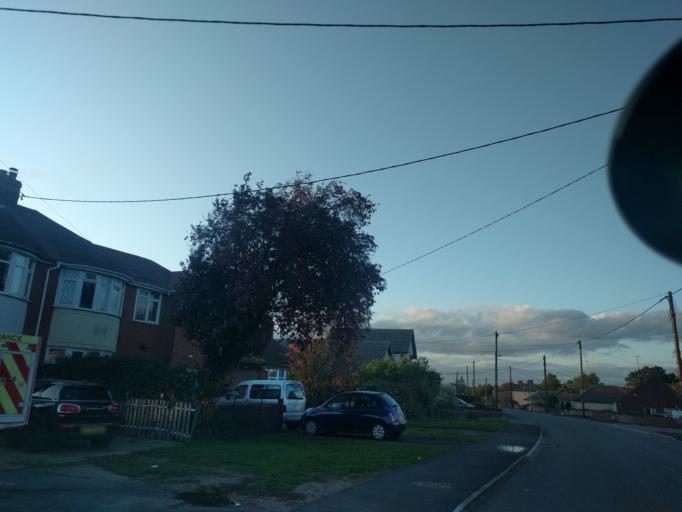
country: GB
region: England
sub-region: Essex
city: Rayne
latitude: 51.8713
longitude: 0.5800
